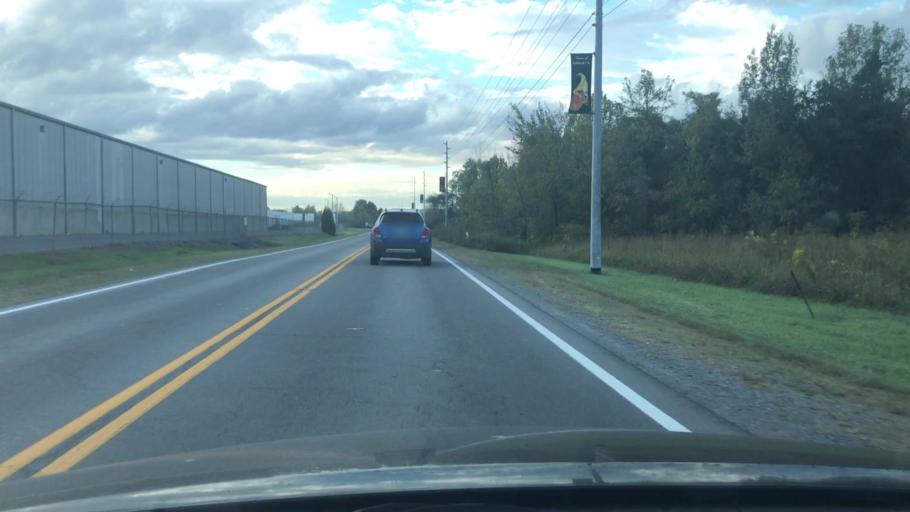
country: US
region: Tennessee
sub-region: Cheatham County
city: Ashland City
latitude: 36.2656
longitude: -87.0669
